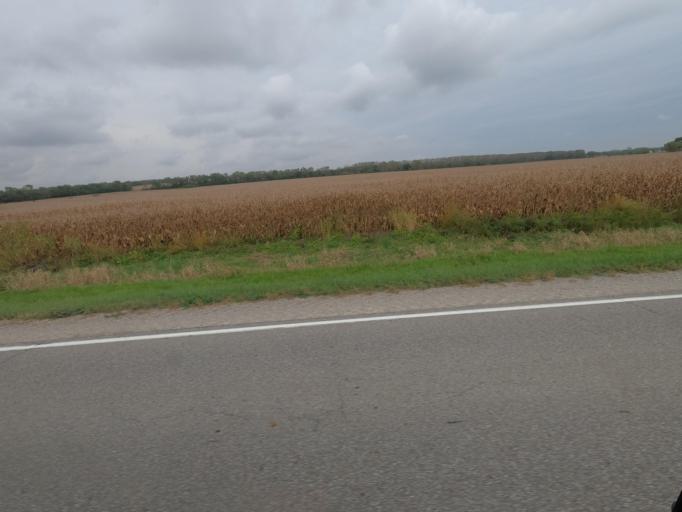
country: US
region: Iowa
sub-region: Wapello County
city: Ottumwa
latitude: 40.9104
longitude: -92.2100
